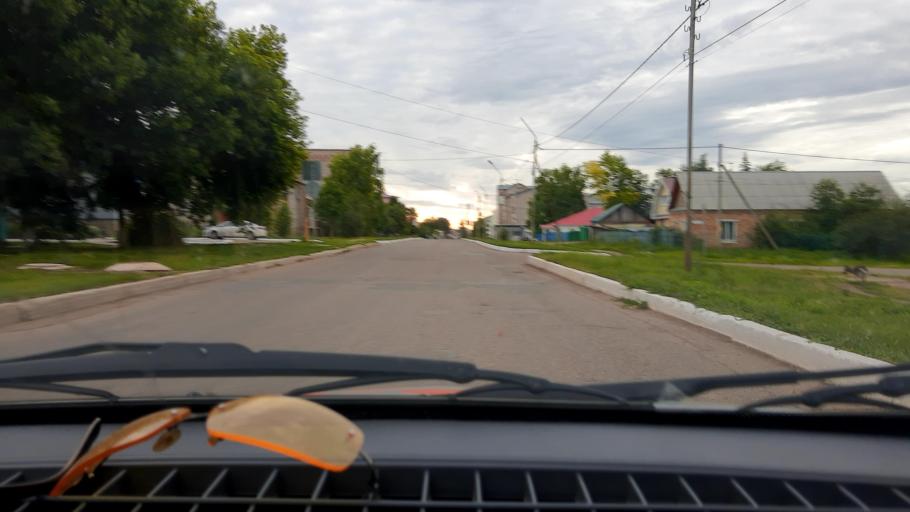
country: RU
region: Bashkortostan
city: Chishmy
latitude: 54.5875
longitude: 55.3849
